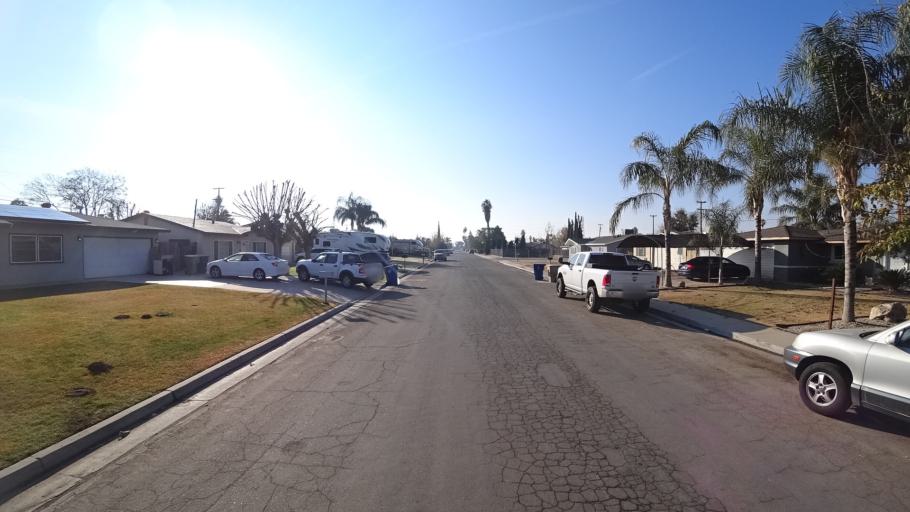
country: US
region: California
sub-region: Kern County
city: Greenfield
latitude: 35.3151
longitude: -119.0075
